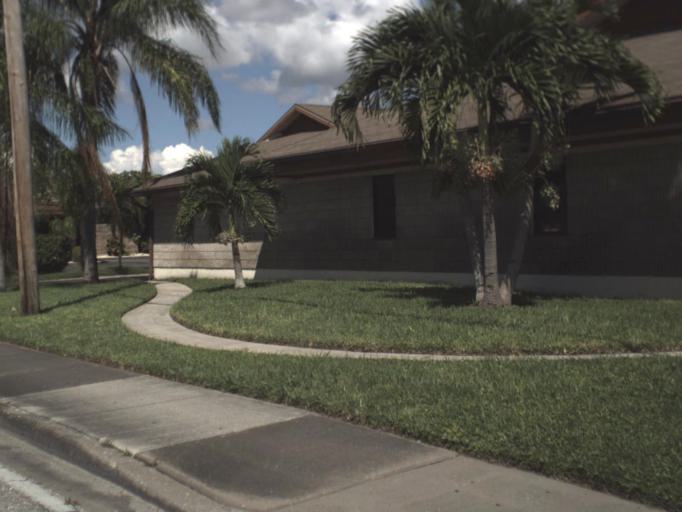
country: US
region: Florida
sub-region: Lee County
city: Lochmoor Waterway Estates
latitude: 26.6402
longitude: -81.9408
